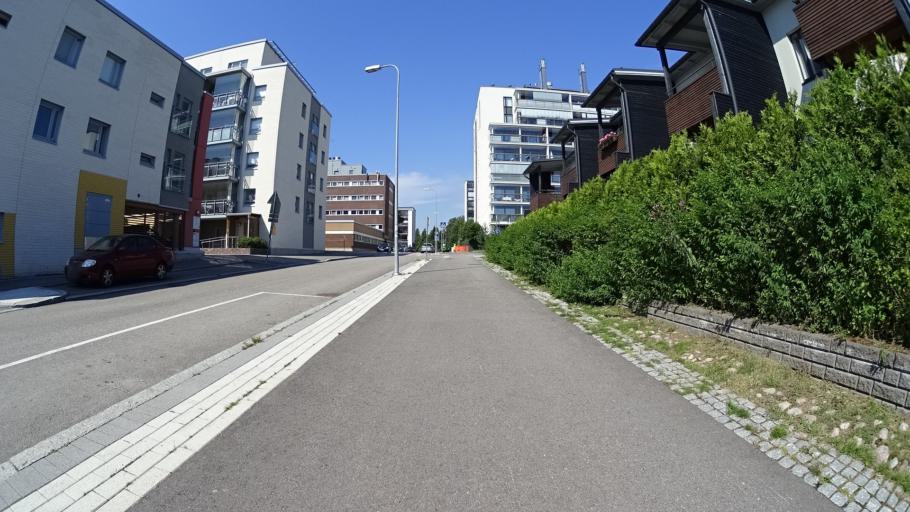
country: FI
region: Uusimaa
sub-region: Helsinki
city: Teekkarikylae
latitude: 60.2217
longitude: 24.8353
